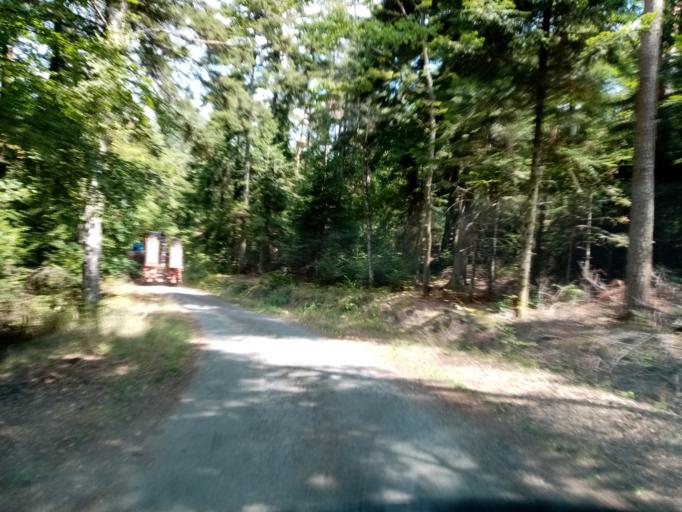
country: FR
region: Alsace
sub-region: Departement du Bas-Rhin
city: Dambach-la-Ville
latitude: 48.3392
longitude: 7.3904
